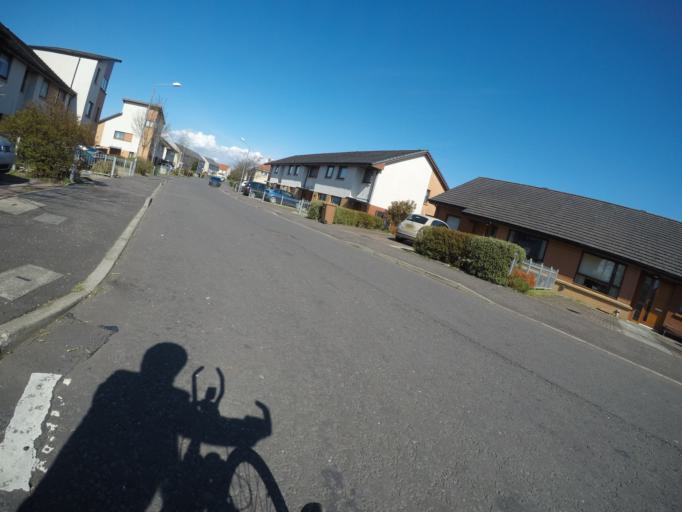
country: GB
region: Scotland
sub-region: North Ayrshire
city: Irvine
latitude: 55.6227
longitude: -4.6656
